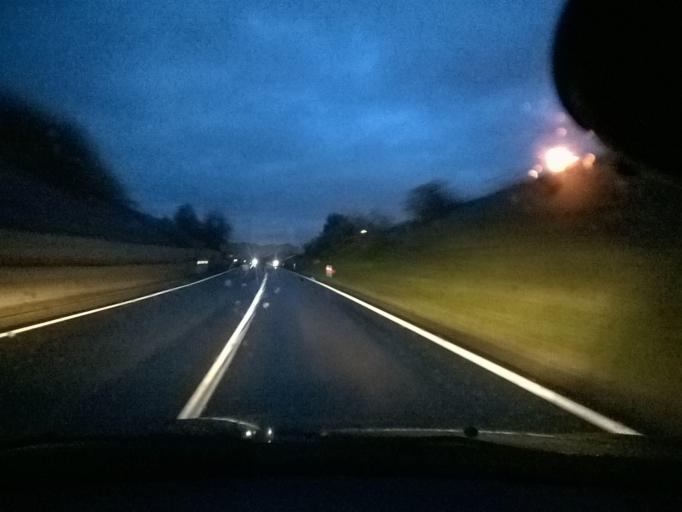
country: HR
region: Krapinsko-Zagorska
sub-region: Grad Krapina
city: Krapina
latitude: 46.1345
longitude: 15.8832
